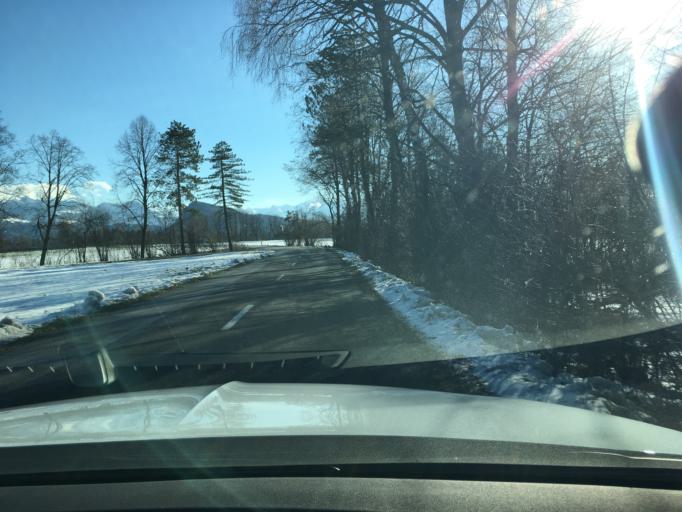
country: CH
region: Saint Gallen
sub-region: Wahlkreis Rheintal
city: Rebstein
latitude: 47.3692
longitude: 9.5927
